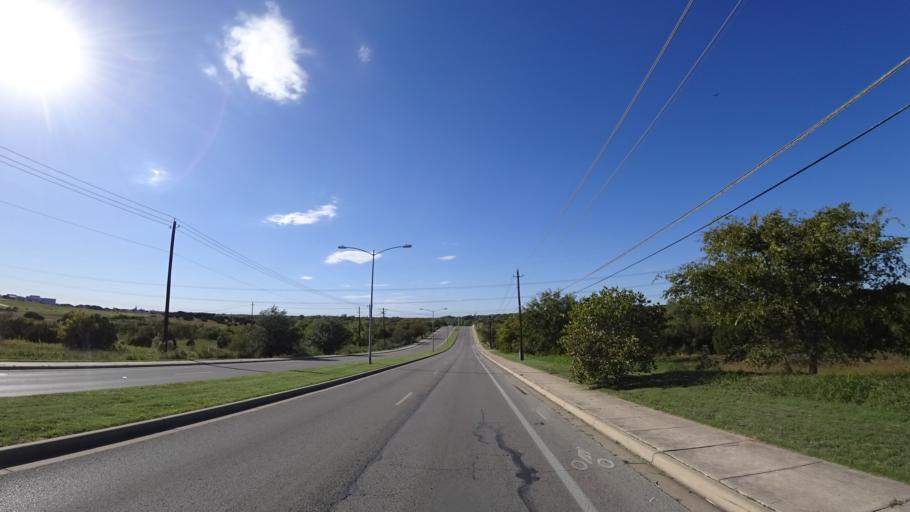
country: US
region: Texas
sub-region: Travis County
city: Hornsby Bend
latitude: 30.2955
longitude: -97.6366
